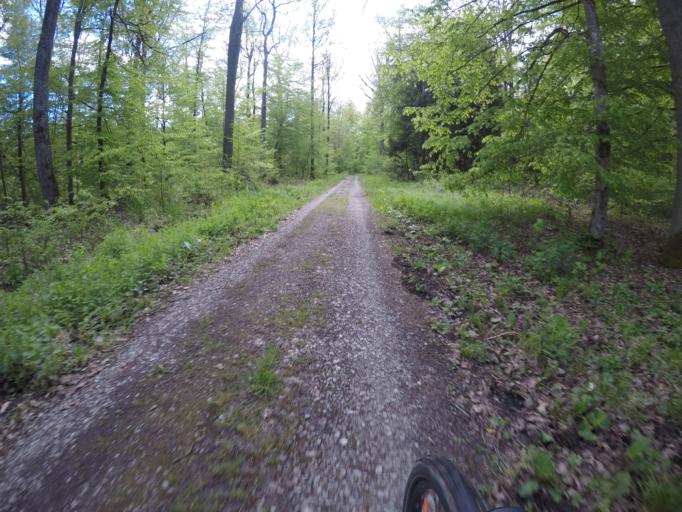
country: DE
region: Baden-Wuerttemberg
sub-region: Regierungsbezirk Stuttgart
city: Nufringen
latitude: 48.5939
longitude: 8.9217
